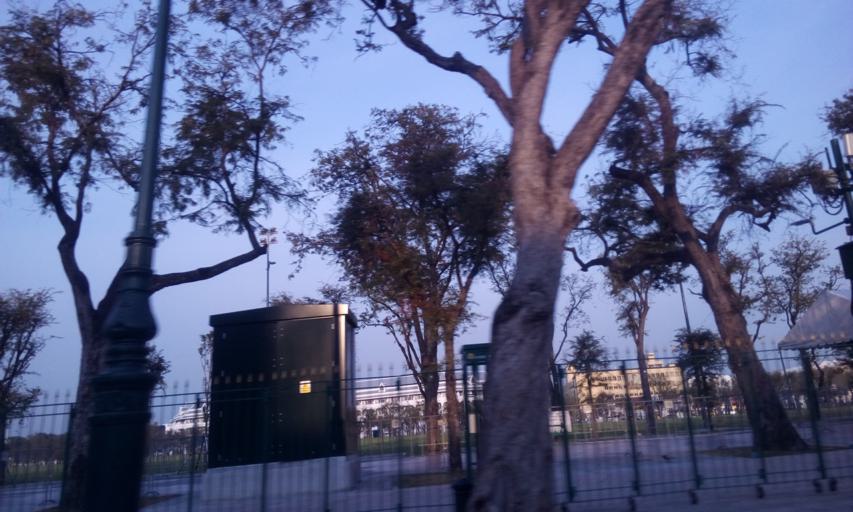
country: TH
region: Bangkok
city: Bangkok
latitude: 13.7533
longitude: 100.4916
